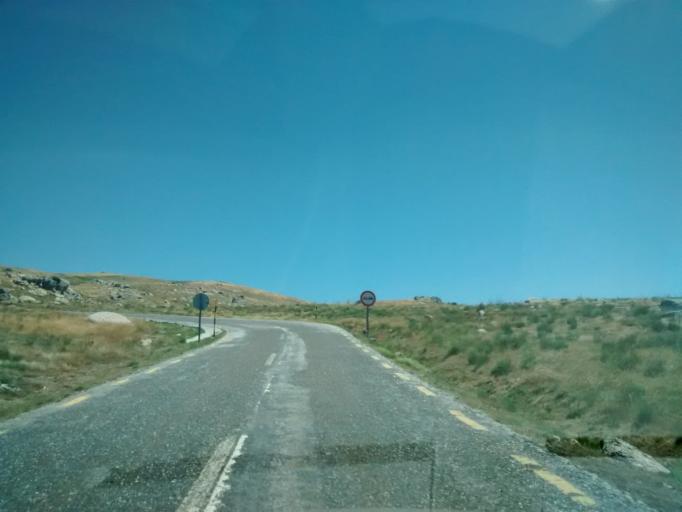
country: PT
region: Guarda
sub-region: Seia
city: Seia
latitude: 40.4136
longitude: -7.6405
